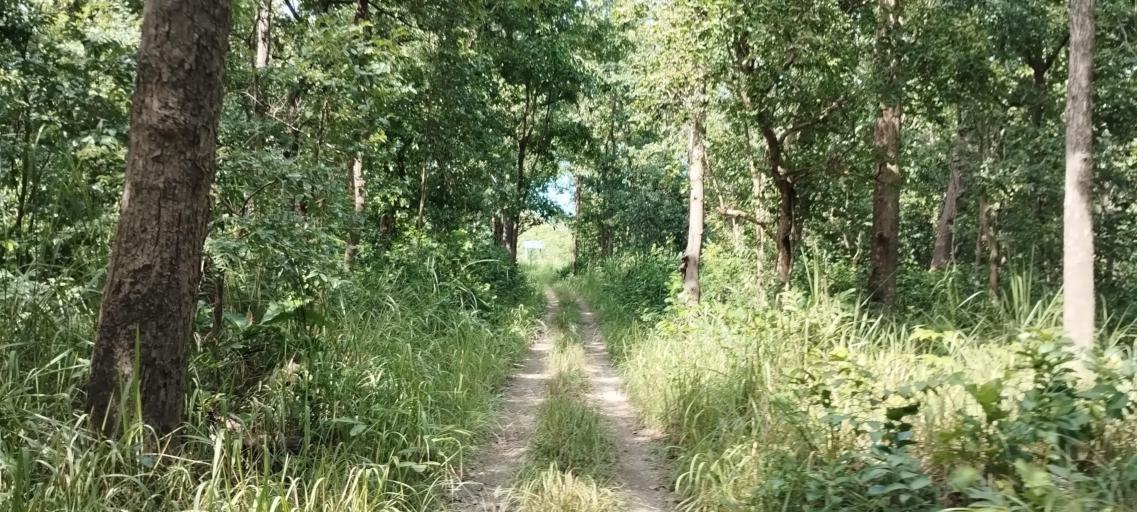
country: NP
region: Far Western
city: Tikapur
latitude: 28.5587
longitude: 81.2943
